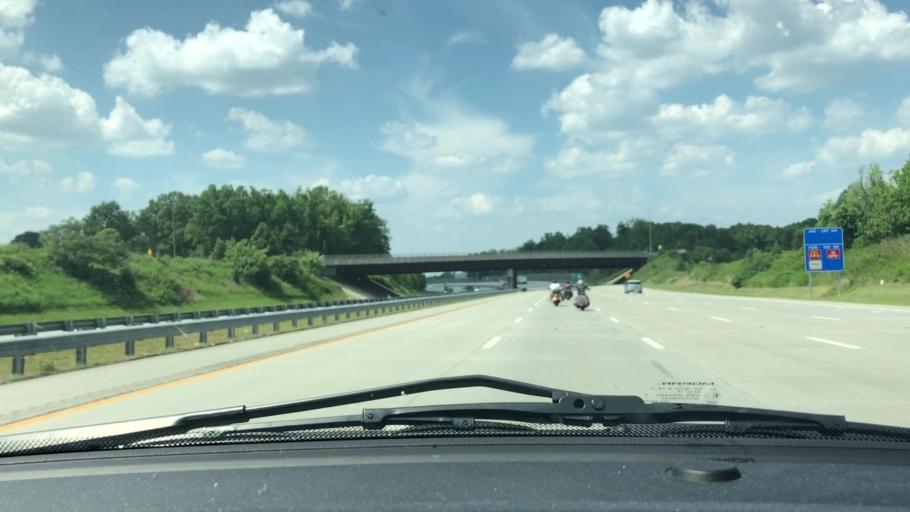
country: US
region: North Carolina
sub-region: Guilford County
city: Jamestown
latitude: 36.0130
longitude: -79.8530
